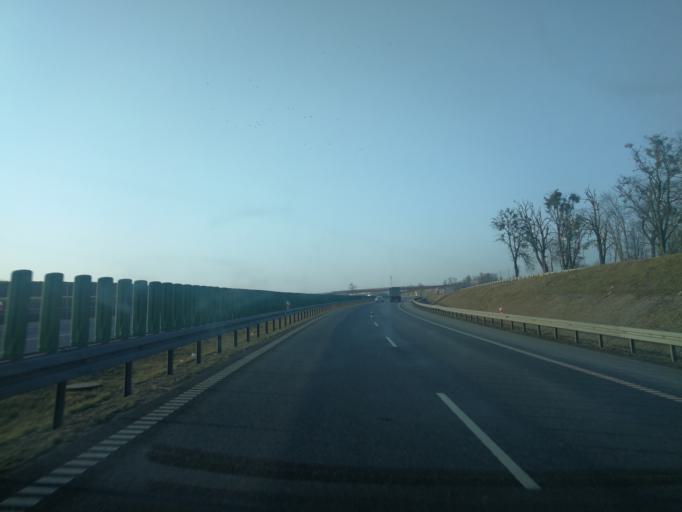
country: PL
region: Warmian-Masurian Voivodeship
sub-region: Powiat elblaski
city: Gronowo Gorne
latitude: 54.1112
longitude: 19.4858
